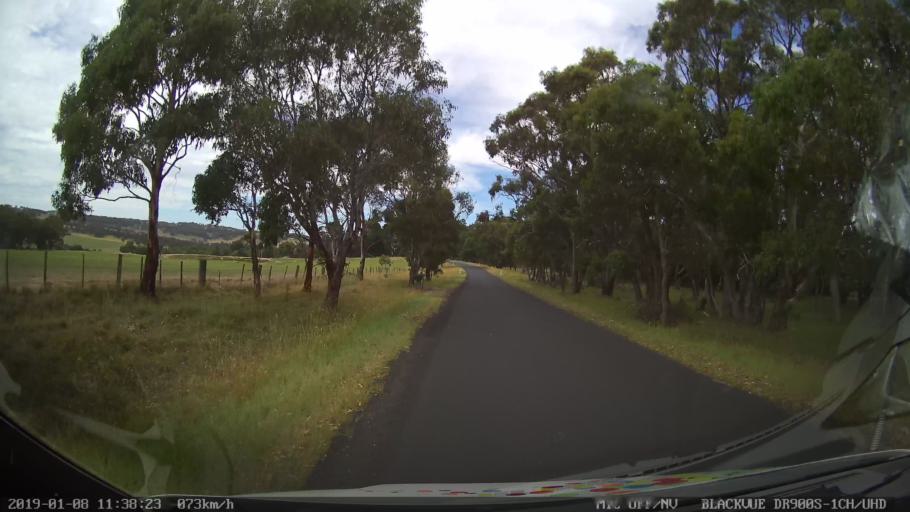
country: AU
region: New South Wales
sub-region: Guyra
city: Guyra
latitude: -30.3603
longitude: 151.5551
